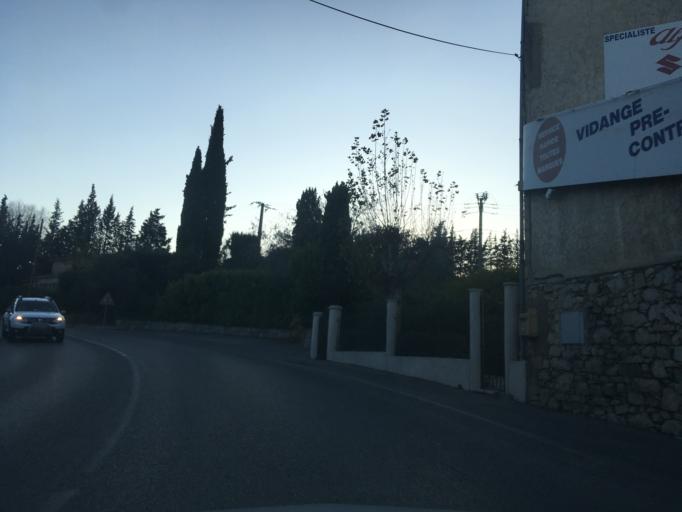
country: FR
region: Provence-Alpes-Cote d'Azur
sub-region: Departement des Alpes-Maritimes
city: Peymeinade
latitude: 43.6384
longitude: 6.8651
